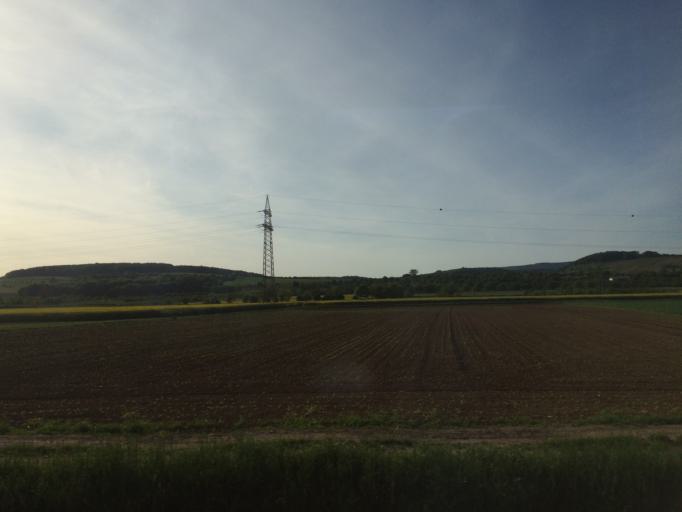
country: DE
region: Hesse
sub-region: Regierungsbezirk Darmstadt
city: Walluf
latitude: 50.0462
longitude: 8.1672
